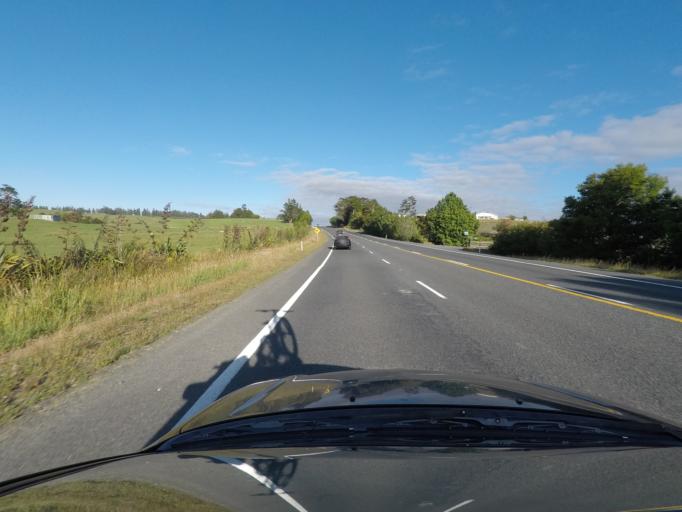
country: NZ
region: Northland
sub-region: Far North District
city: Kawakawa
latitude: -35.5126
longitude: 174.1842
